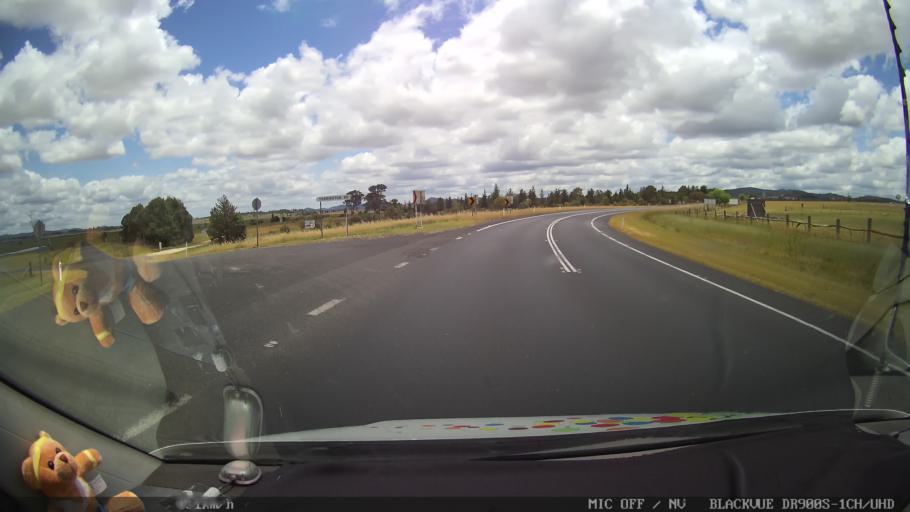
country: AU
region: New South Wales
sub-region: Glen Innes Severn
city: Glen Innes
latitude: -29.4356
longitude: 151.8471
